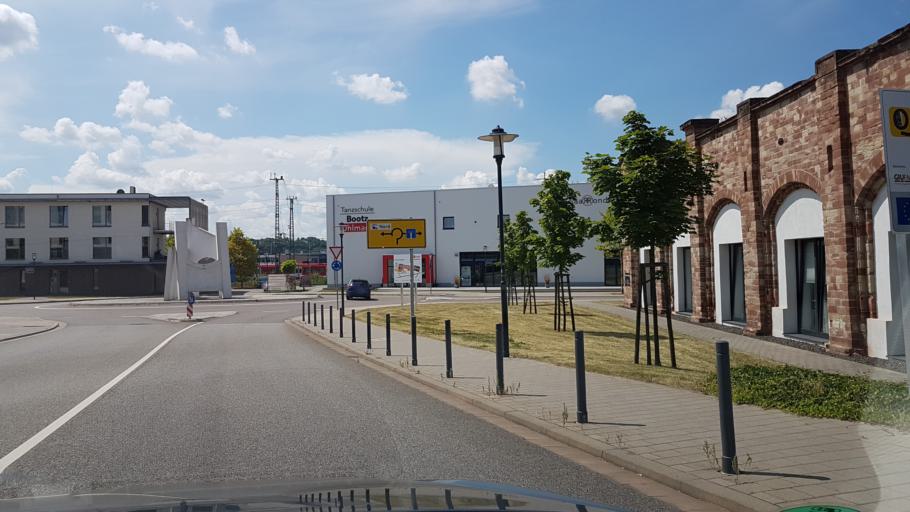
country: DE
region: Saarland
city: Saarbrucken
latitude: 49.2432
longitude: 6.9856
